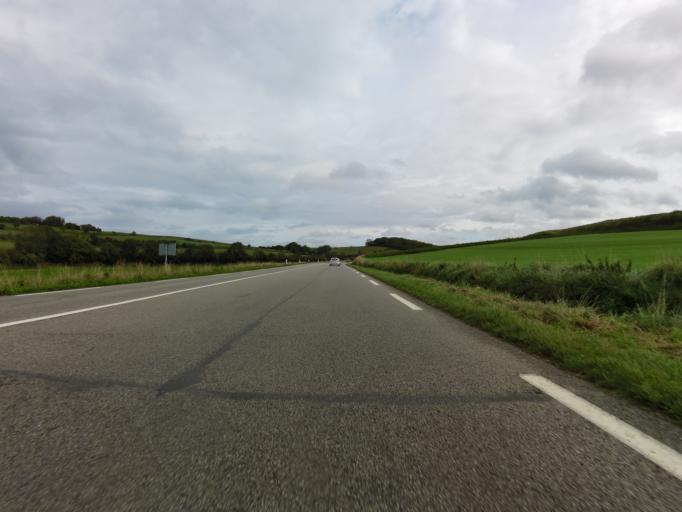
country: FR
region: Haute-Normandie
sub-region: Departement de la Seine-Maritime
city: Criel-sur-Mer
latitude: 50.0228
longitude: 1.3271
